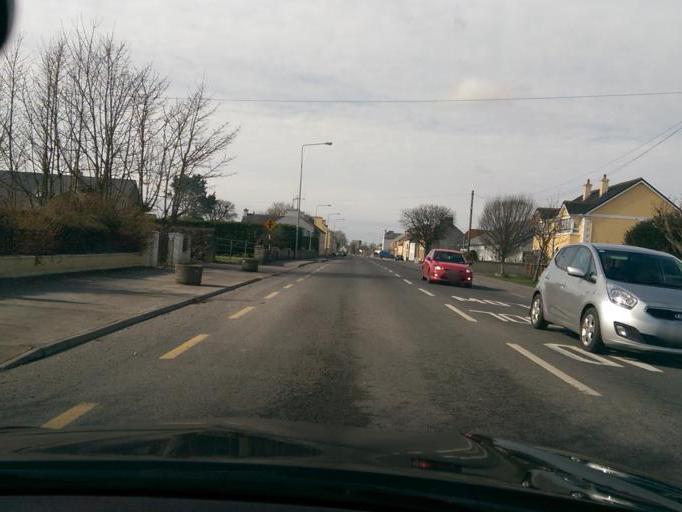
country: IE
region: Connaught
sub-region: County Galway
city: Athenry
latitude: 53.4874
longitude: -8.5645
